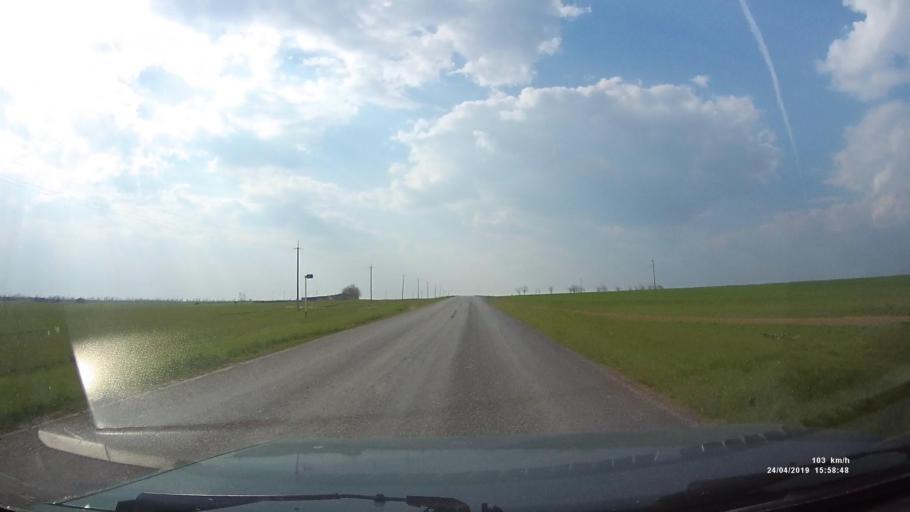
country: RU
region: Kalmykiya
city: Yashalta
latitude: 46.6174
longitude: 42.4839
